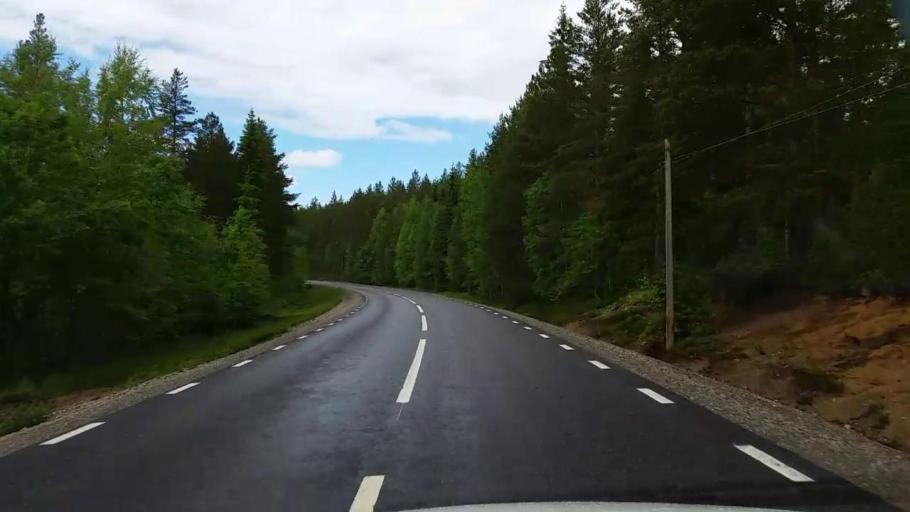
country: SE
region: Gaevleborg
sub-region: Sandvikens Kommun
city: Jarbo
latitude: 60.8632
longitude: 16.4322
